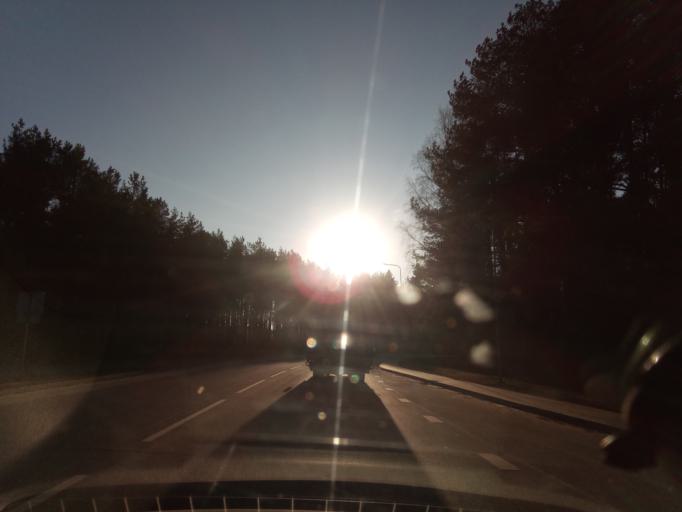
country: LT
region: Alytaus apskritis
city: Druskininkai
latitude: 54.0095
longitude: 23.9917
